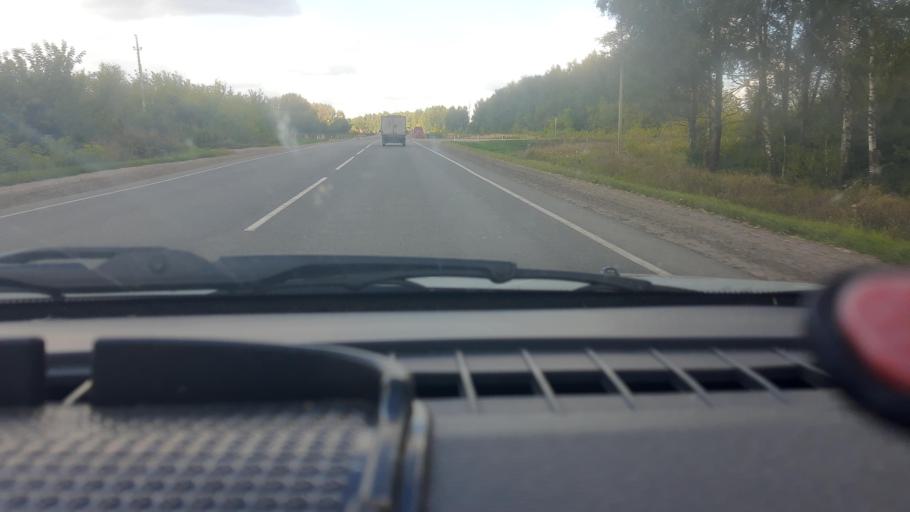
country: RU
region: Nizjnij Novgorod
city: Arzamas
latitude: 55.2932
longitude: 43.9404
